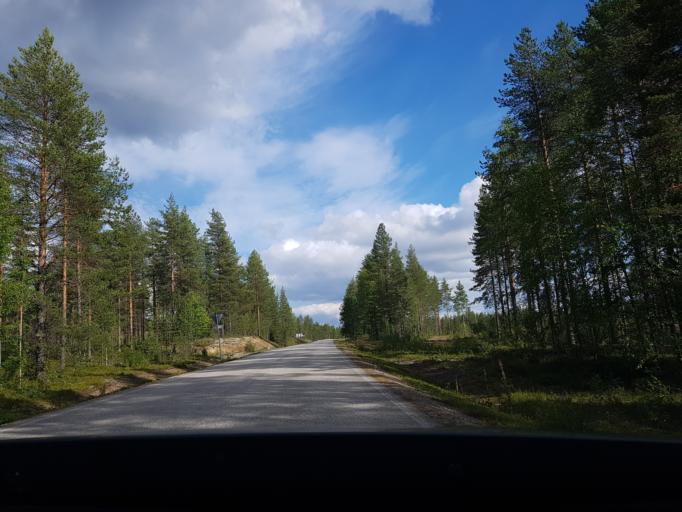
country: FI
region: Kainuu
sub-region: Kehys-Kainuu
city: Kuhmo
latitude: 64.6211
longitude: 29.6998
